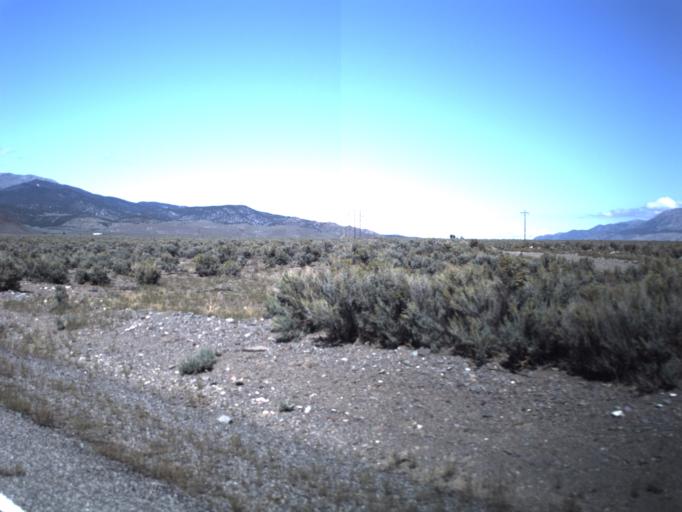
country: US
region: Utah
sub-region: Piute County
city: Junction
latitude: 38.2454
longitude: -112.2341
